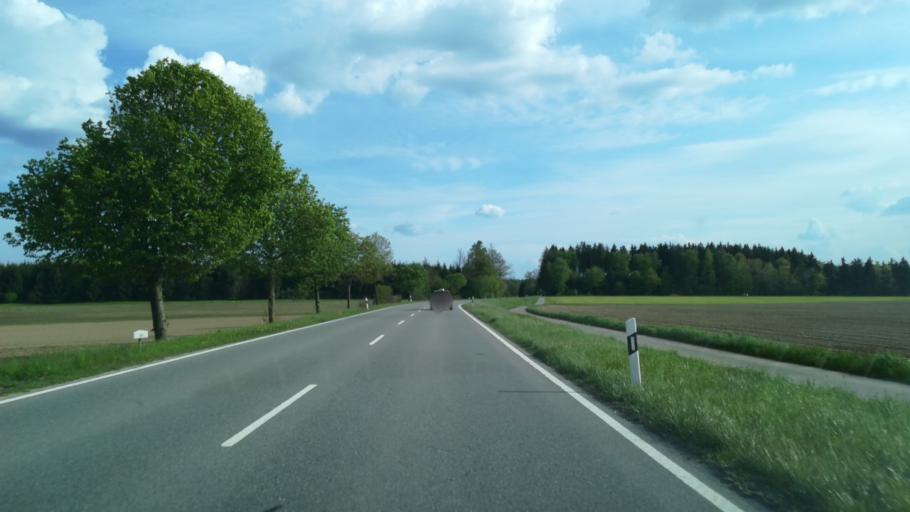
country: DE
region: Baden-Wuerttemberg
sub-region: Freiburg Region
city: Muhlingen
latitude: 47.9492
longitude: 9.0448
